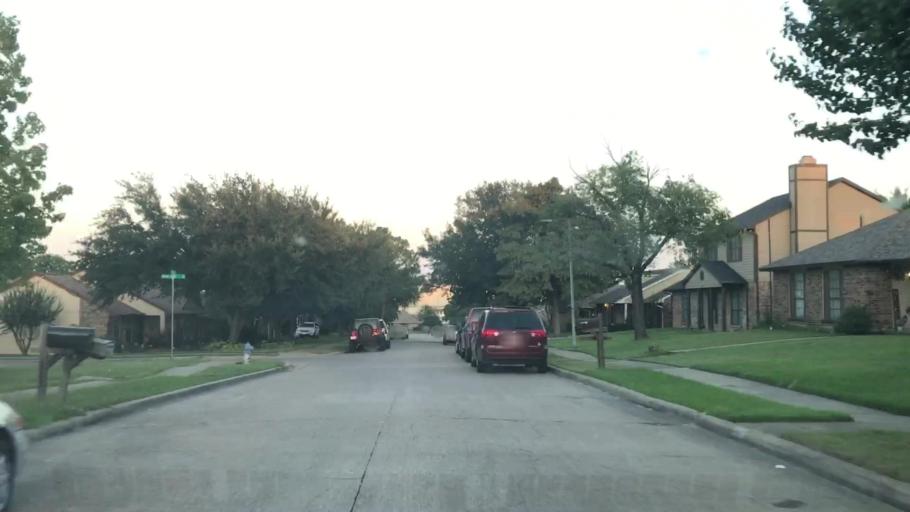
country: US
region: Texas
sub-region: Dallas County
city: Mesquite
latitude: 32.7617
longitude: -96.6304
